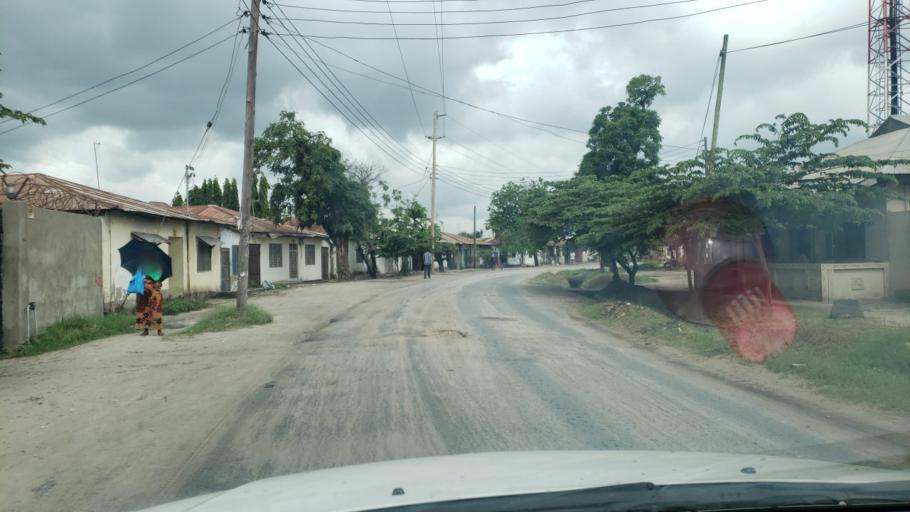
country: TZ
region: Dar es Salaam
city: Magomeni
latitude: -6.8086
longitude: 39.2476
